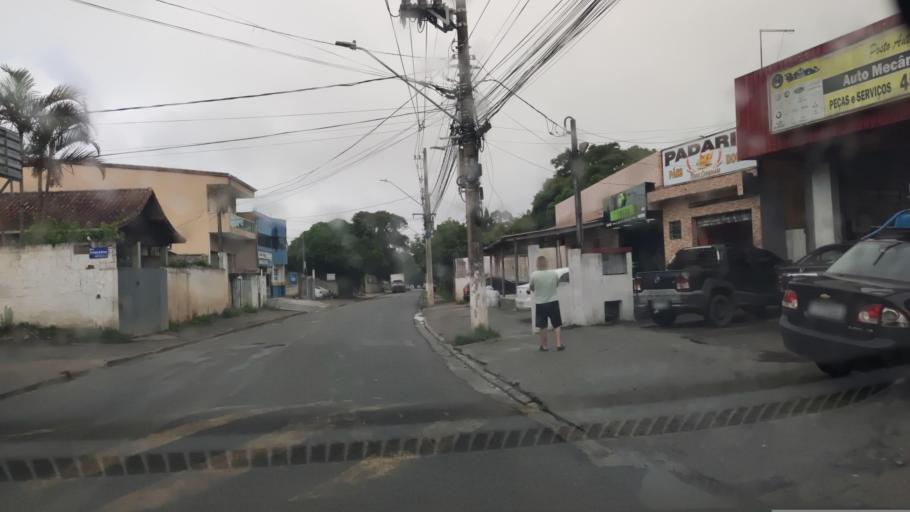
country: BR
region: Sao Paulo
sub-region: Vargem Grande Paulista
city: Vargem Grande Paulista
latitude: -23.6819
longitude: -47.0273
